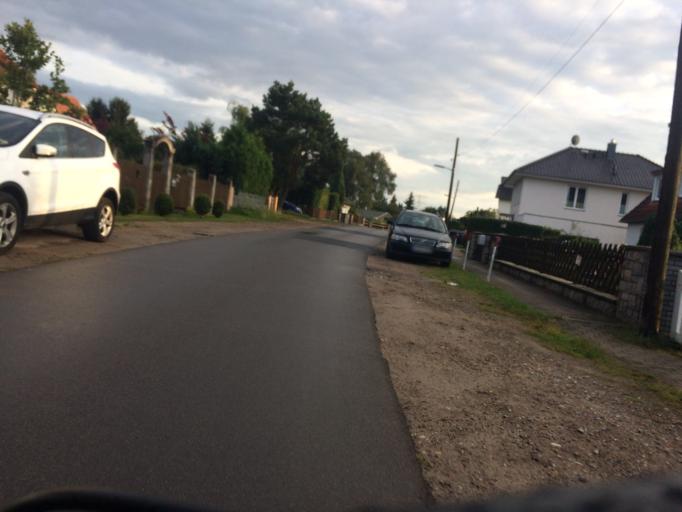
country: DE
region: Berlin
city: Heinersdorf
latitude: 52.5723
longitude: 13.4565
